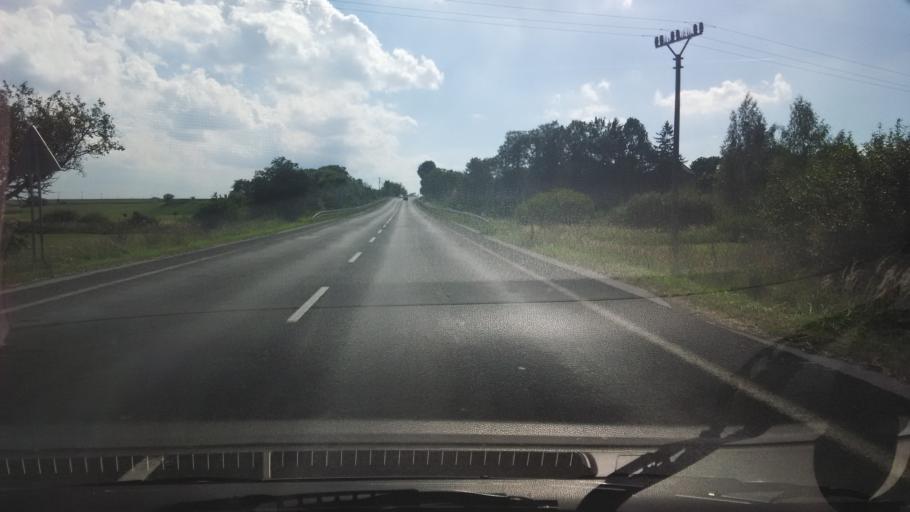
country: SK
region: Zilinsky
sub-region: Okres Martin
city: Martin
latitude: 48.9615
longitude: 18.9041
